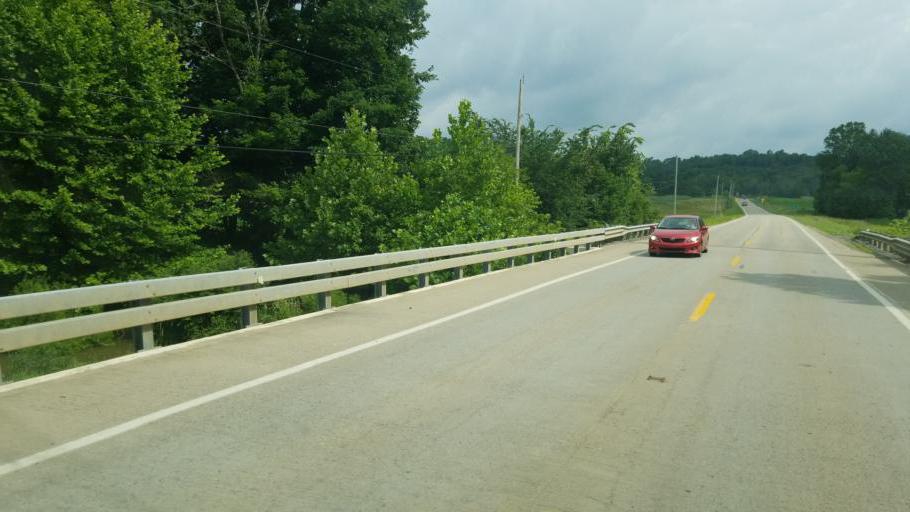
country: US
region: Ohio
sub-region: Columbiana County
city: Lisbon
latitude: 40.7022
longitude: -80.8076
